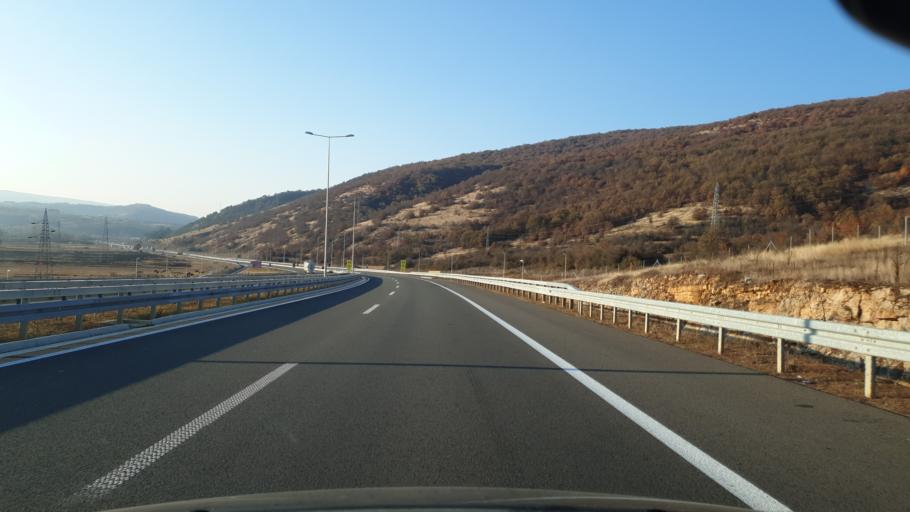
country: RS
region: Central Serbia
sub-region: Pirotski Okrug
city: Dimitrovgrad
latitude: 43.0183
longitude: 22.7481
